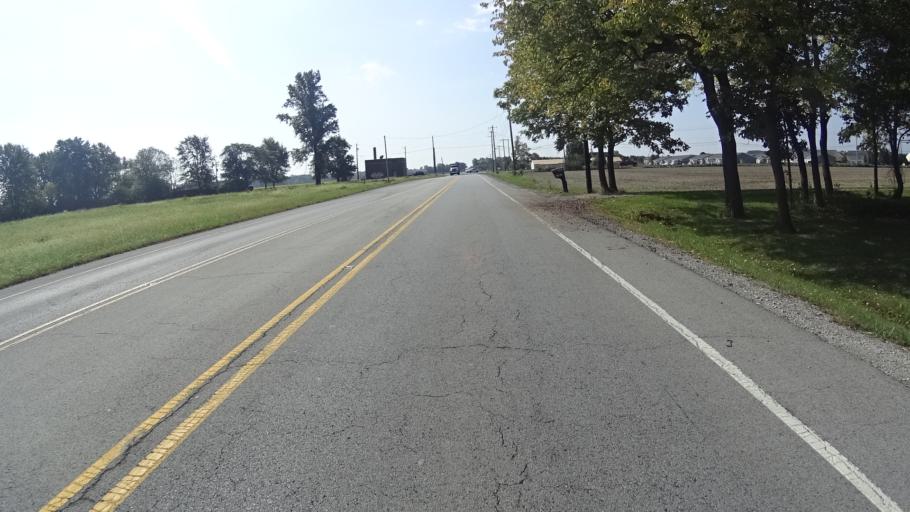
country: US
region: Indiana
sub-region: Madison County
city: Ingalls
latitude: 39.9896
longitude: -85.8432
